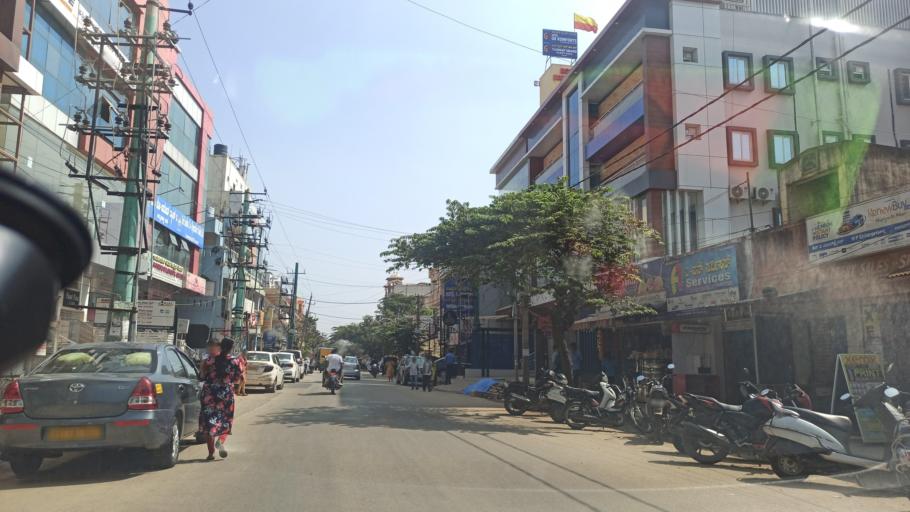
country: IN
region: Karnataka
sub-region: Bangalore Urban
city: Yelahanka
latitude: 13.0667
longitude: 77.5959
